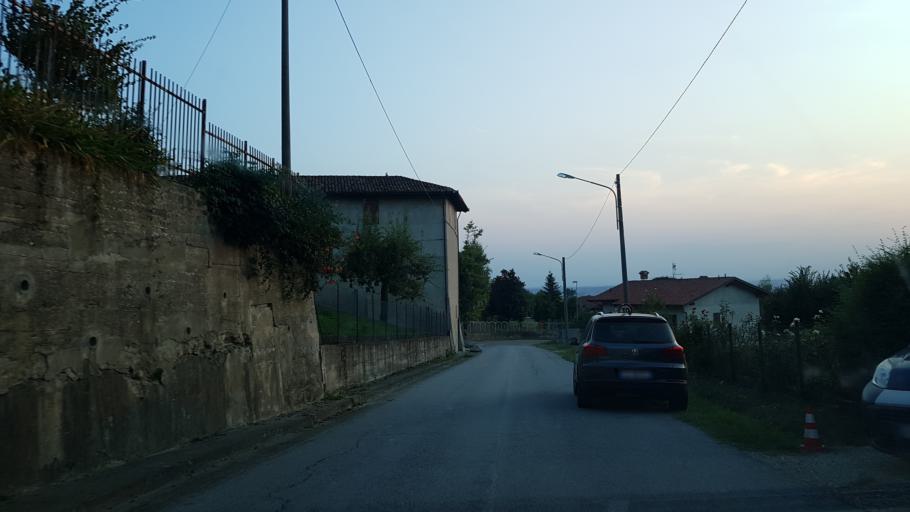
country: IT
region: Piedmont
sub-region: Provincia di Cuneo
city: Novello
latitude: 44.5872
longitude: 7.9261
